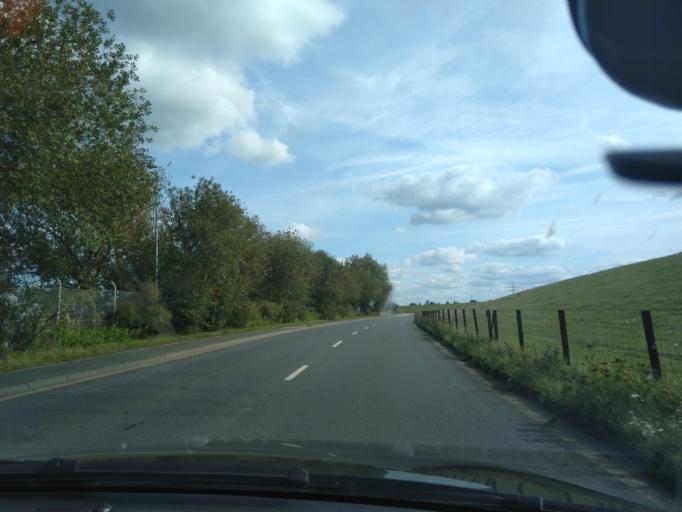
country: DE
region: Lower Saxony
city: Leer
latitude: 53.2141
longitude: 7.4563
